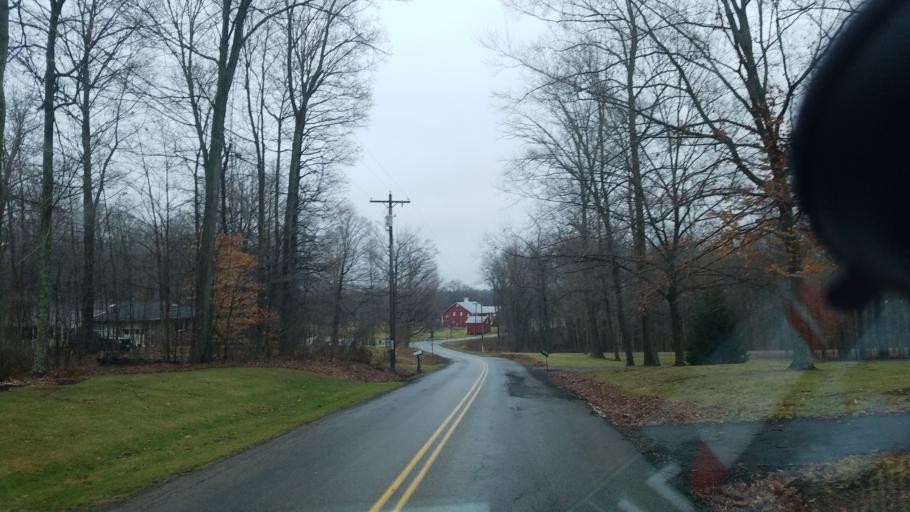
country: US
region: Ohio
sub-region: Knox County
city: Fredericktown
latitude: 40.4946
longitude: -82.5670
